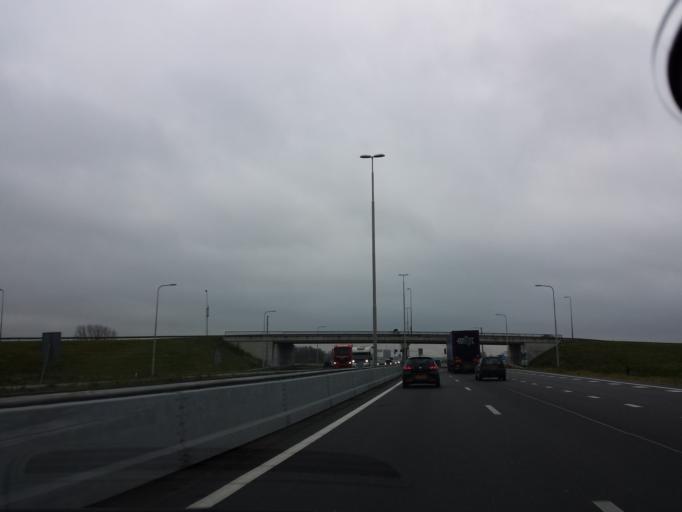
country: NL
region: Limburg
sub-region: Gemeente Sittard-Geleen
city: Born
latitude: 51.0741
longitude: 5.8247
